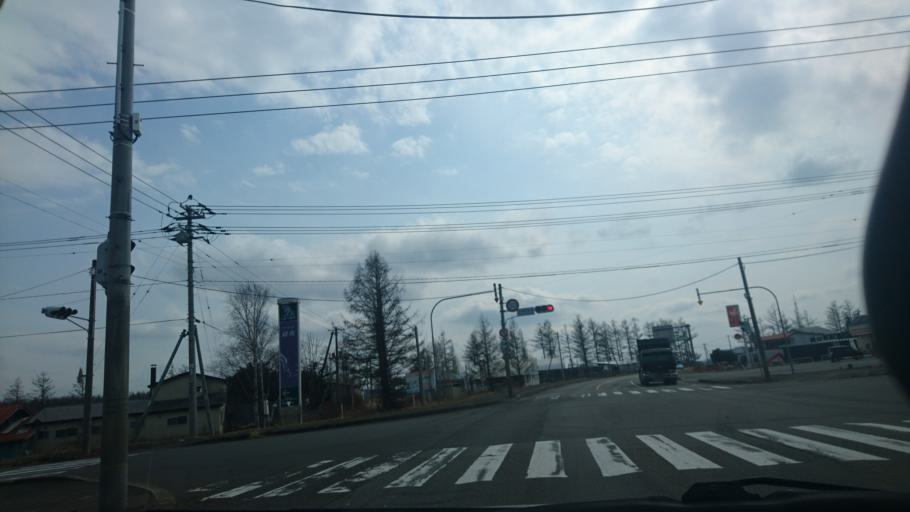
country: JP
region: Hokkaido
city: Otofuke
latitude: 43.1674
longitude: 143.2663
